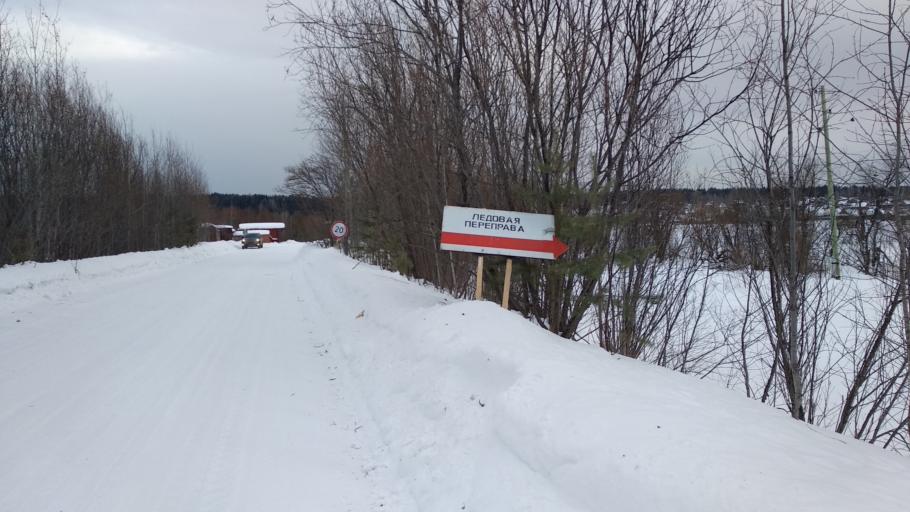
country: RU
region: Sverdlovsk
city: Serov
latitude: 59.8472
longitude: 60.7168
